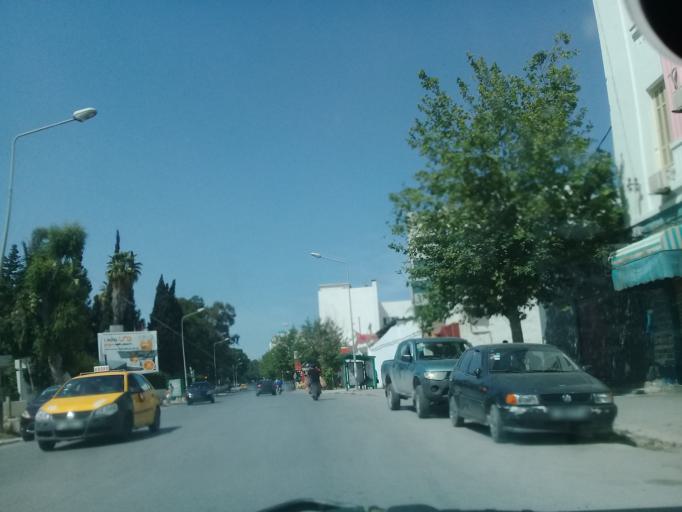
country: TN
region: Tunis
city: Tunis
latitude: 36.8134
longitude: 10.1750
